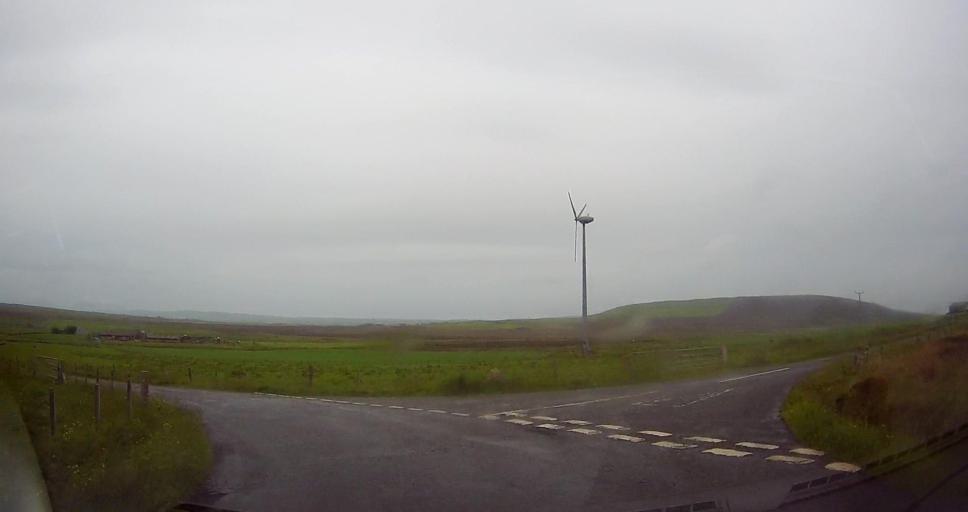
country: GB
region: Scotland
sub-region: Orkney Islands
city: Stromness
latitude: 59.0936
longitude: -3.1823
